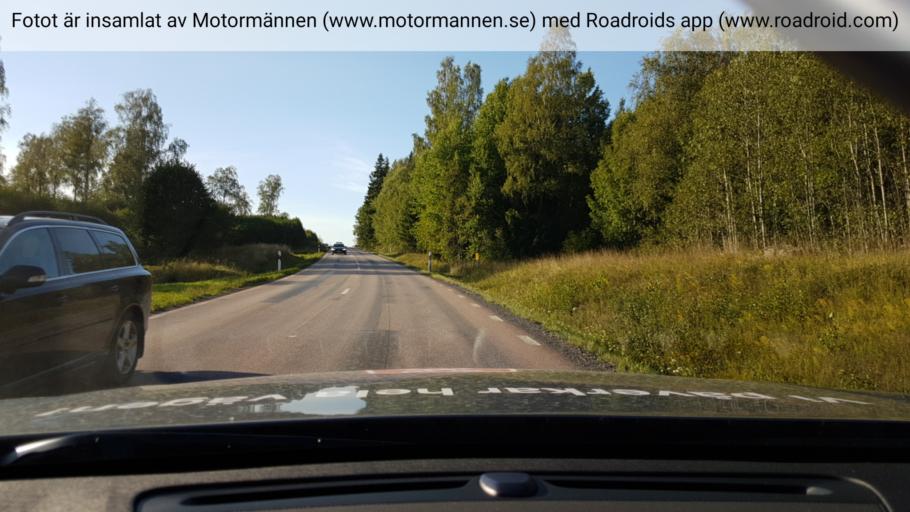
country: SE
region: Vaestmanland
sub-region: Kopings Kommun
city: Kolsva
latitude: 59.6143
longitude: 15.8262
